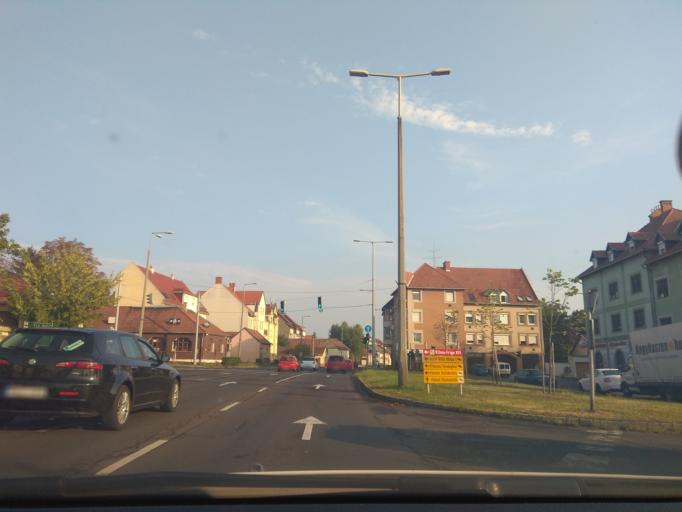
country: HU
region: Heves
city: Eger
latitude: 47.8958
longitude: 20.3685
